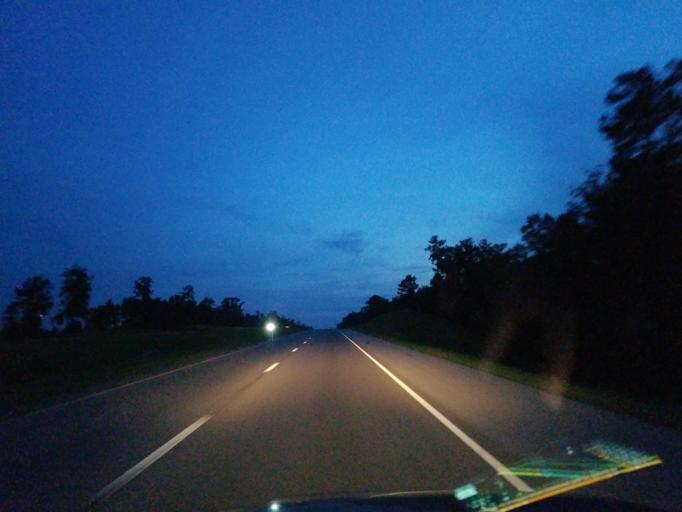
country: US
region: Mississippi
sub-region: Jones County
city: Ellisville
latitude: 31.5659
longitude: -89.2535
